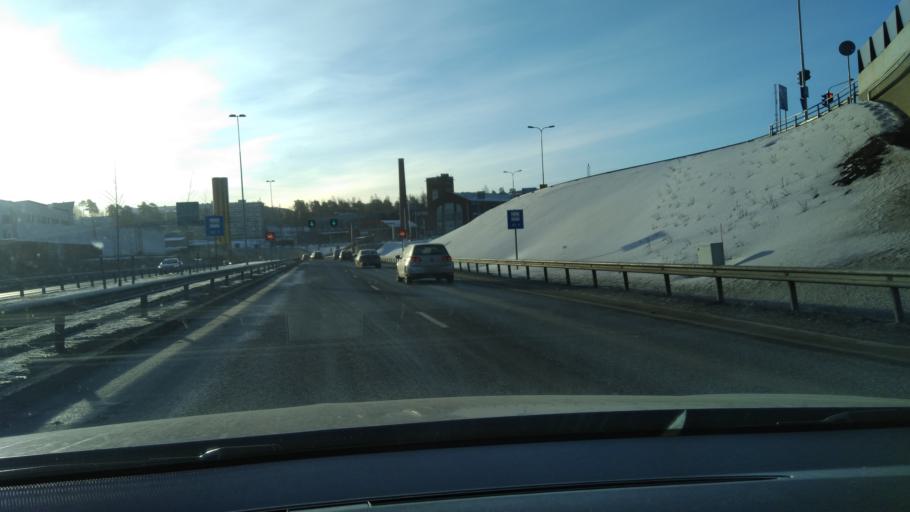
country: FI
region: Pirkanmaa
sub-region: Tampere
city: Tampere
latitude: 61.5029
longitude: 23.7260
